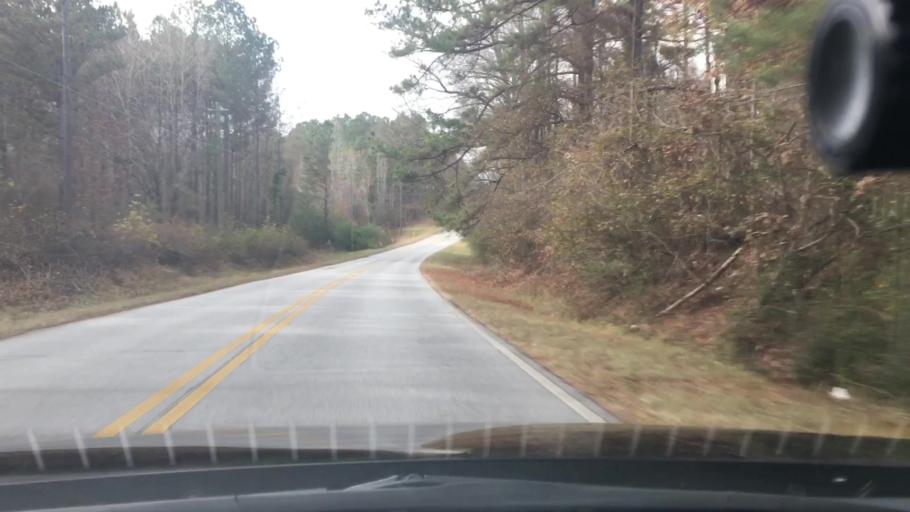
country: US
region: Georgia
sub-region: Spalding County
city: Experiment
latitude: 33.2728
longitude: -84.3561
